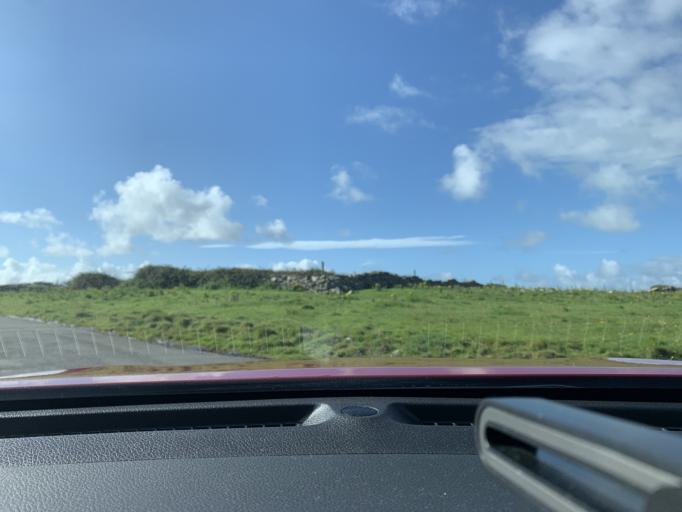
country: IE
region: Connaught
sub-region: Sligo
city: Strandhill
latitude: 54.3975
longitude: -8.5666
